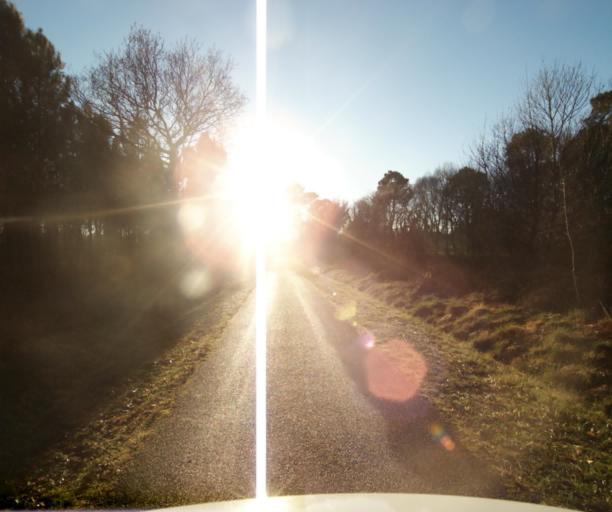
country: FR
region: Aquitaine
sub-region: Departement des Landes
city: Gabarret
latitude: 44.1002
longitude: -0.0836
